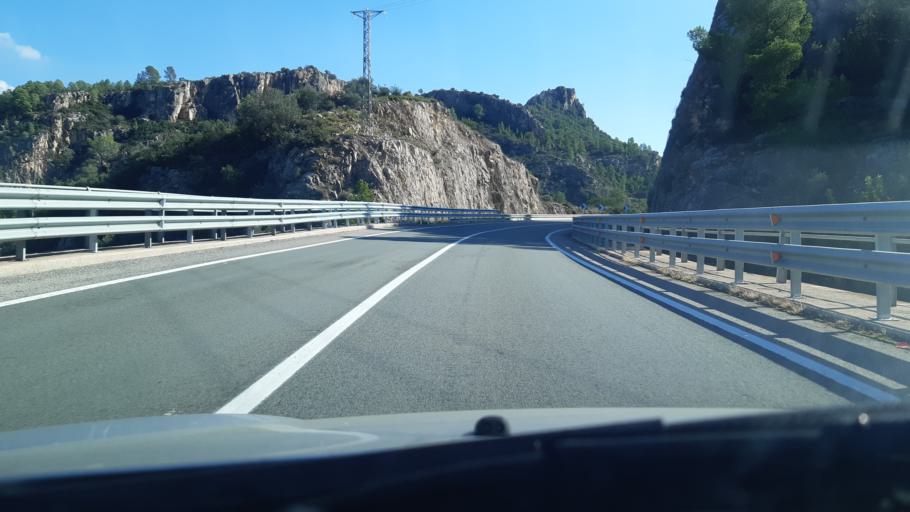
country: ES
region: Catalonia
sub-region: Provincia de Tarragona
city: Tivenys
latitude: 40.9422
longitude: 0.4880
